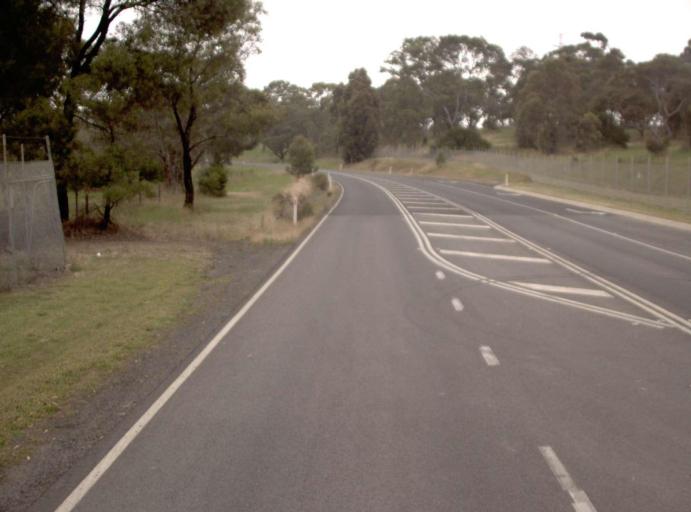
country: AU
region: Victoria
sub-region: Latrobe
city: Morwell
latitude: -38.2759
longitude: 146.3873
